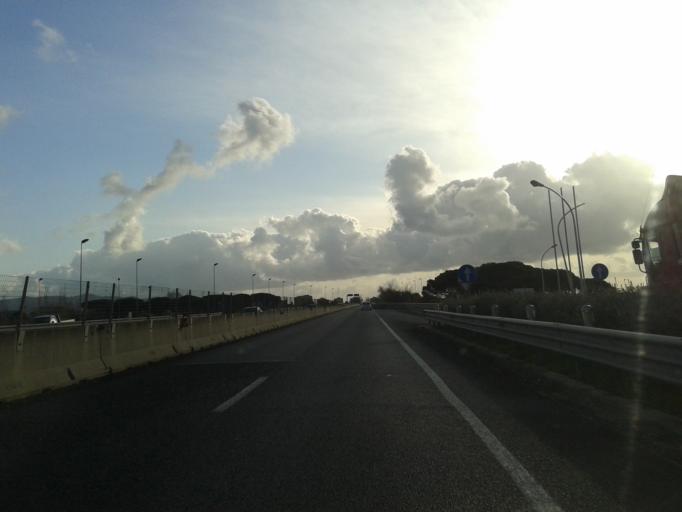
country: IT
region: Tuscany
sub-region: Provincia di Livorno
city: Livorno
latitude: 43.5508
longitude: 10.3427
